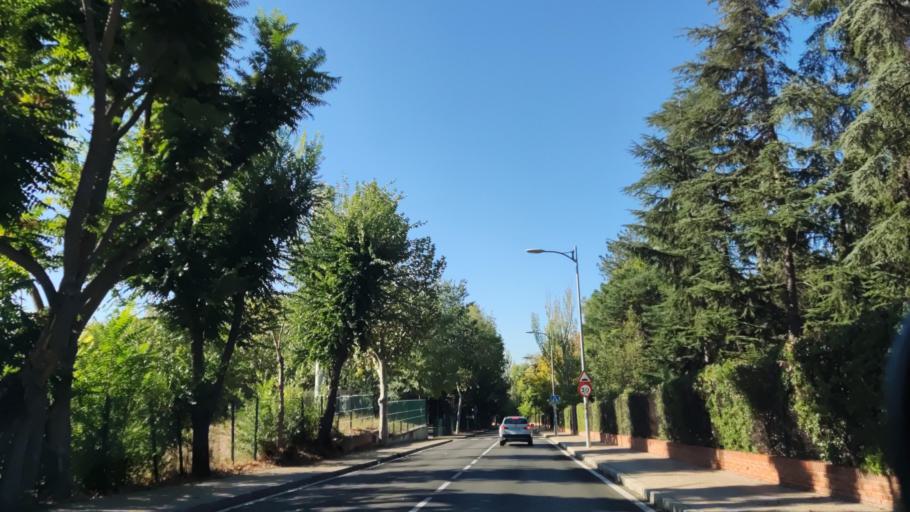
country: ES
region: Madrid
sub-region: Provincia de Madrid
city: Tetuan de las Victorias
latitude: 40.4506
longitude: -3.7198
